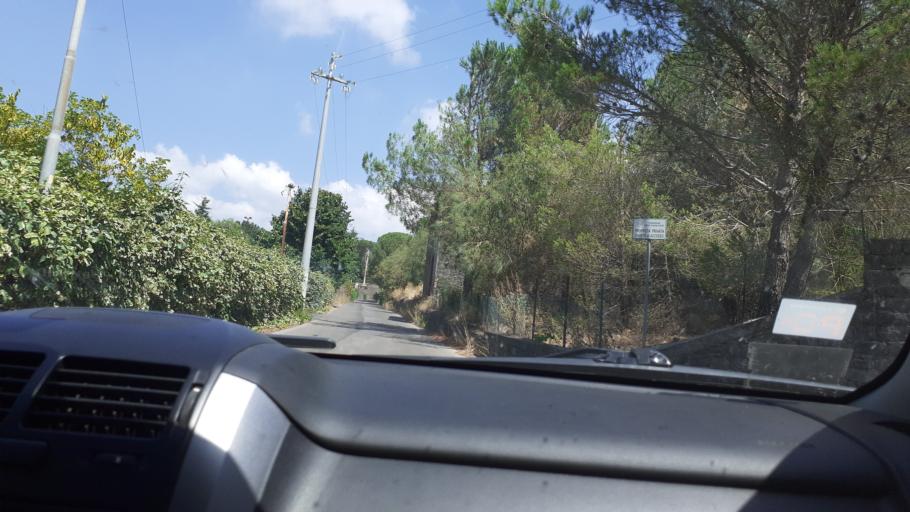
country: IT
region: Sicily
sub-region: Catania
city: Nicolosi
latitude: 37.6274
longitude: 15.0247
